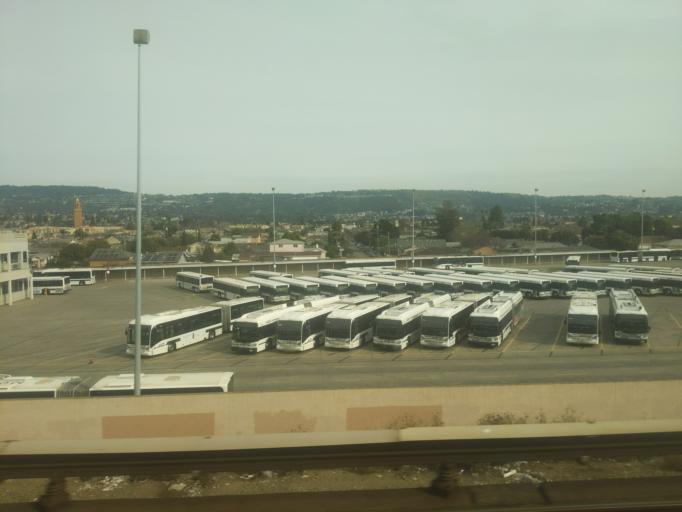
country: US
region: California
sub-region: Alameda County
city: Alameda
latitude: 37.7599
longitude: -122.2044
